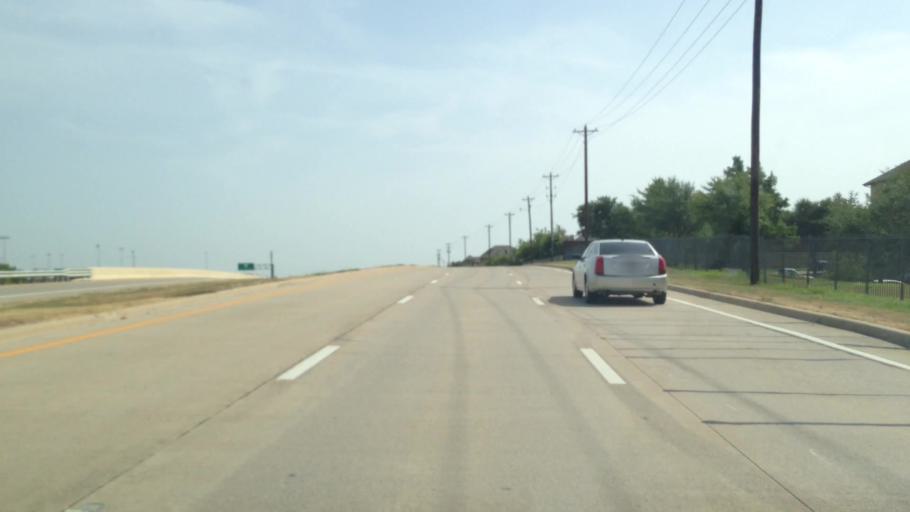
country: US
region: Texas
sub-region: Denton County
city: Lewisville
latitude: 33.0292
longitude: -96.9285
